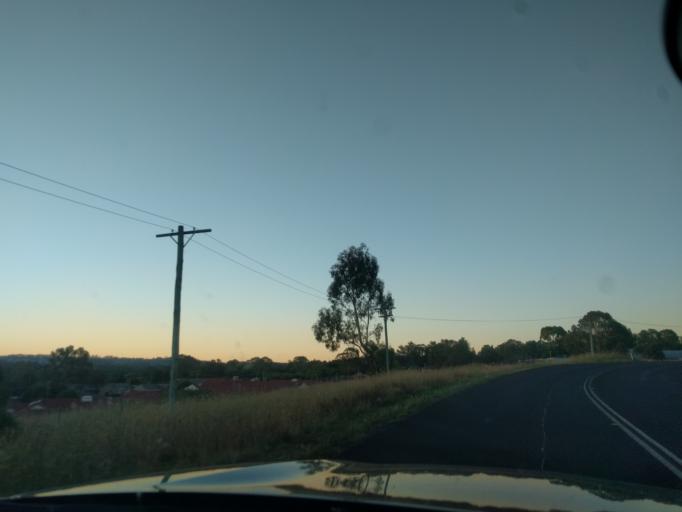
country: AU
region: New South Wales
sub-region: Armidale Dumaresq
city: Armidale
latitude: -30.5036
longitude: 151.6613
